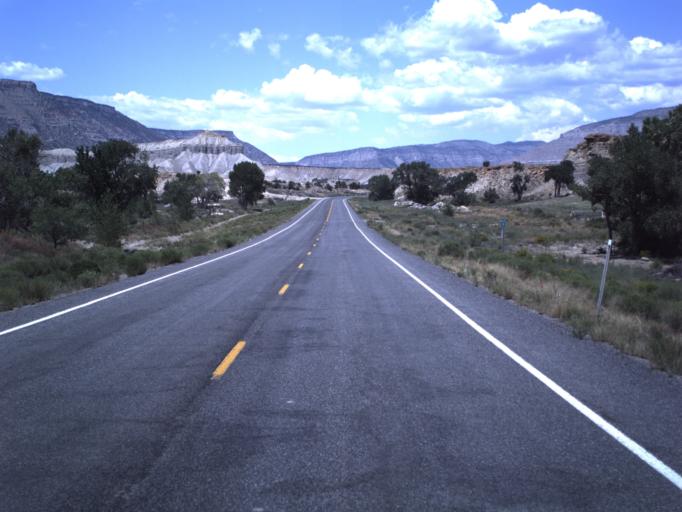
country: US
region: Utah
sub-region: Emery County
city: Orangeville
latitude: 39.2340
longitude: -111.0820
